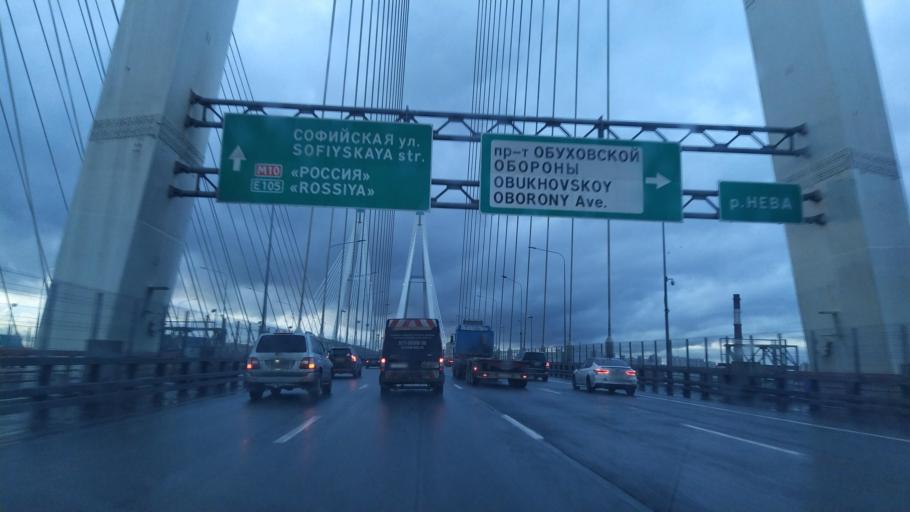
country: RU
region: Leningrad
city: Rybatskoye
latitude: 59.8552
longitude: 30.4940
